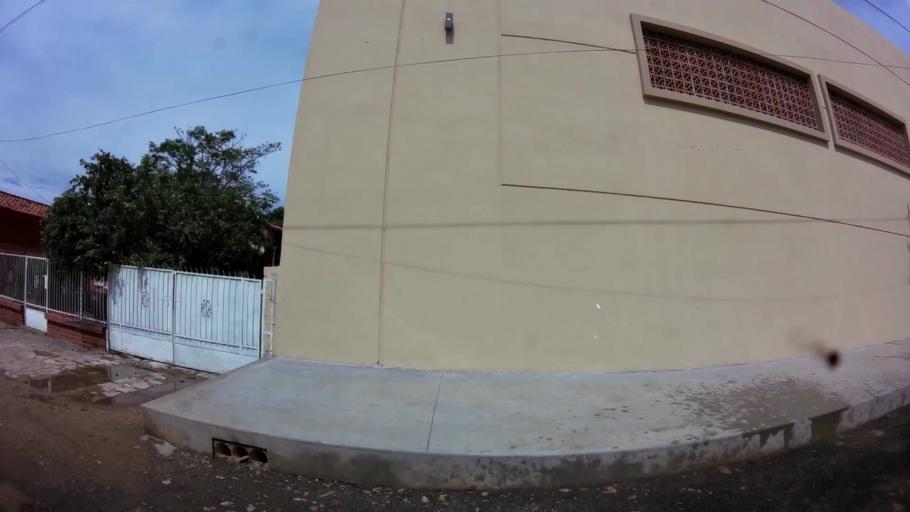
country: PY
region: Central
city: Limpio
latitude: -25.1781
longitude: -57.4804
